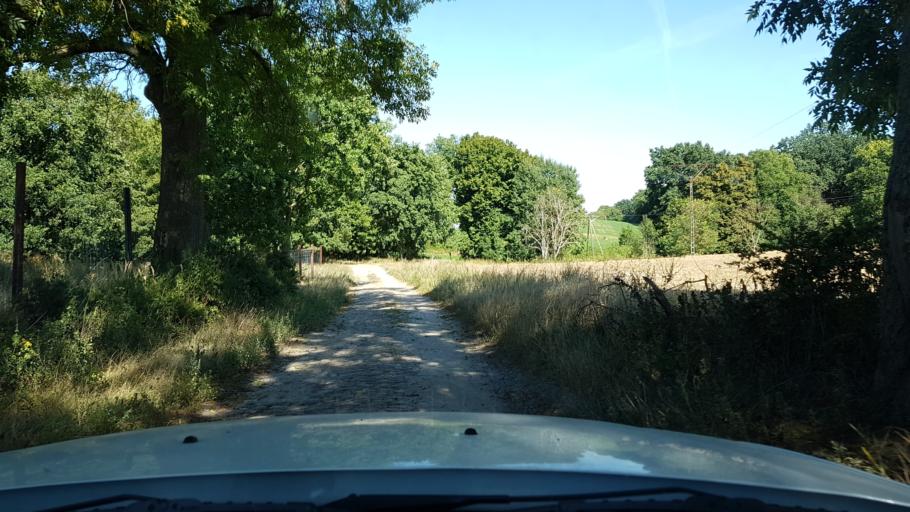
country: PL
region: West Pomeranian Voivodeship
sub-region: Powiat gryfinski
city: Cedynia
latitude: 52.8633
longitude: 14.2281
